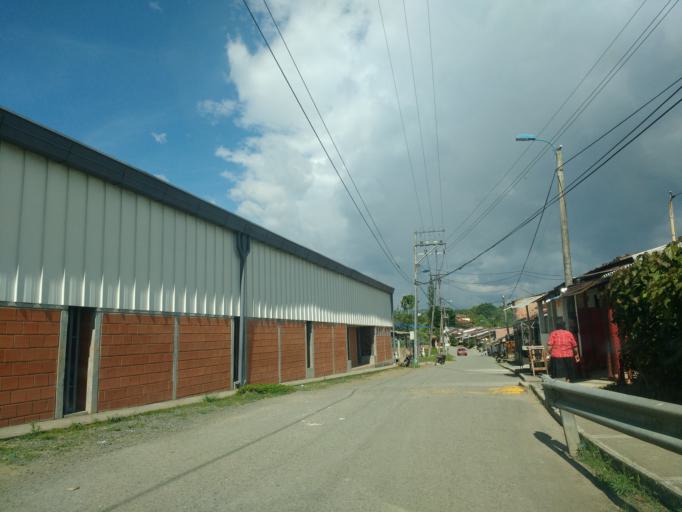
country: CO
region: Valle del Cauca
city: Alcala
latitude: 4.6734
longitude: -75.7739
